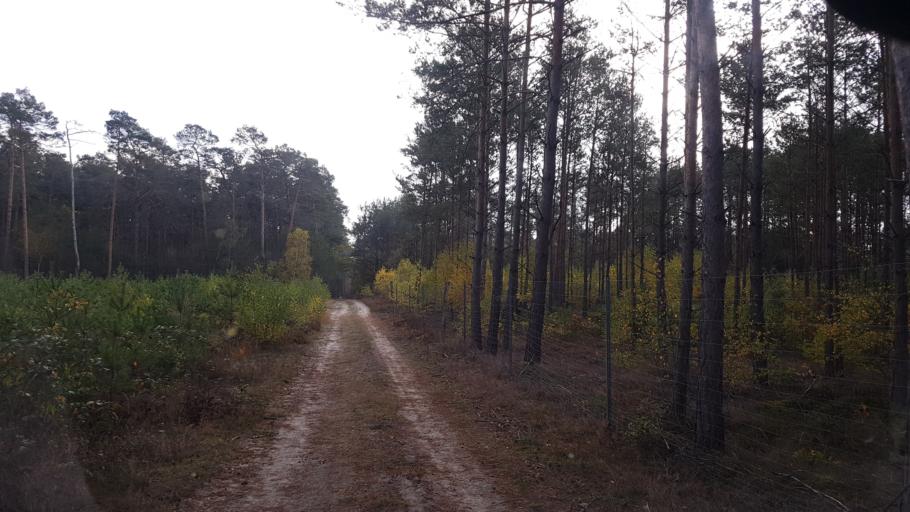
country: DE
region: Brandenburg
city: Schonborn
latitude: 51.6617
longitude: 13.4781
